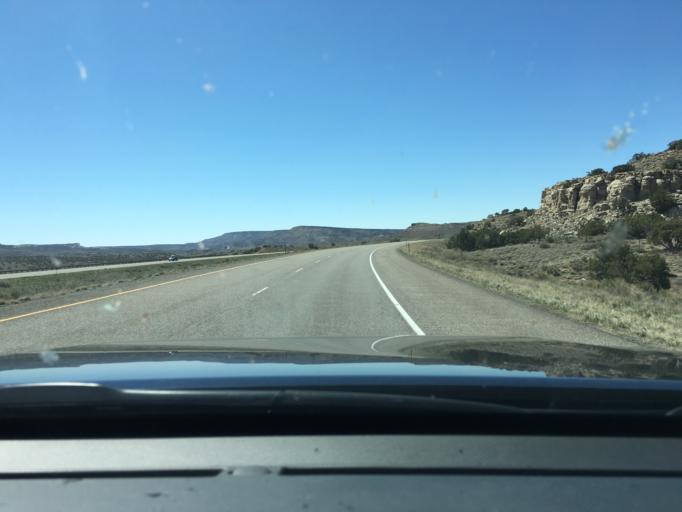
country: US
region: Colorado
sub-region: Mesa County
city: Loma
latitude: 39.2118
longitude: -108.9683
